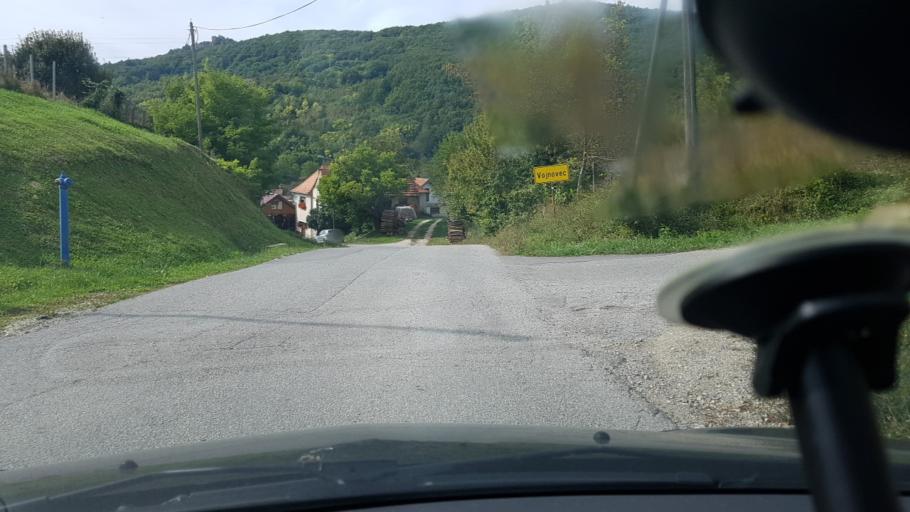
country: HR
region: Varazdinska
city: Ljubescica
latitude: 46.1204
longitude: 16.4279
